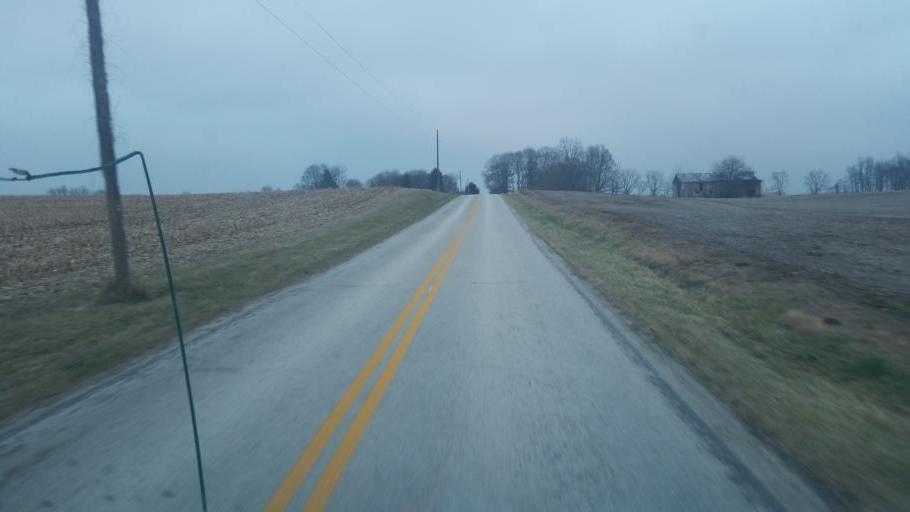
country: US
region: Ohio
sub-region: Seneca County
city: Tiffin
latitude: 40.9929
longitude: -83.2230
